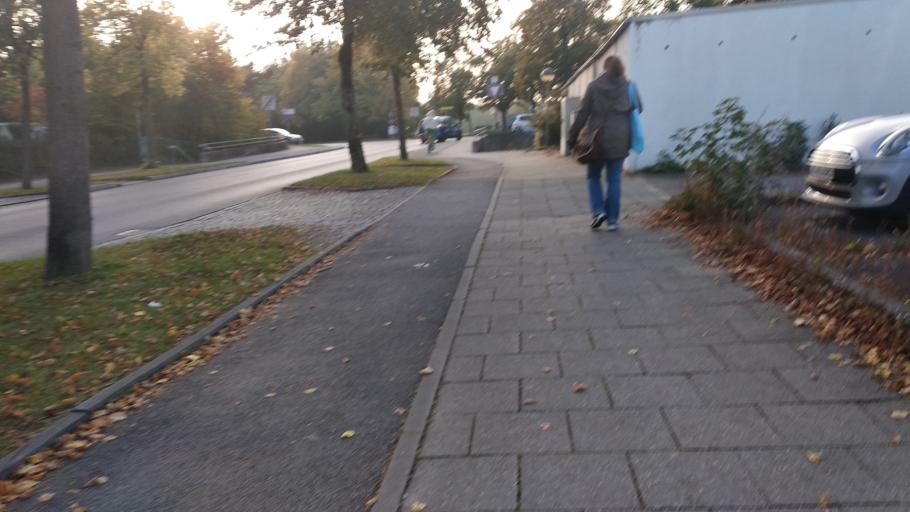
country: DE
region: Bavaria
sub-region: Upper Bavaria
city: Kirchheim bei Muenchen
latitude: 48.1640
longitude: 11.7550
